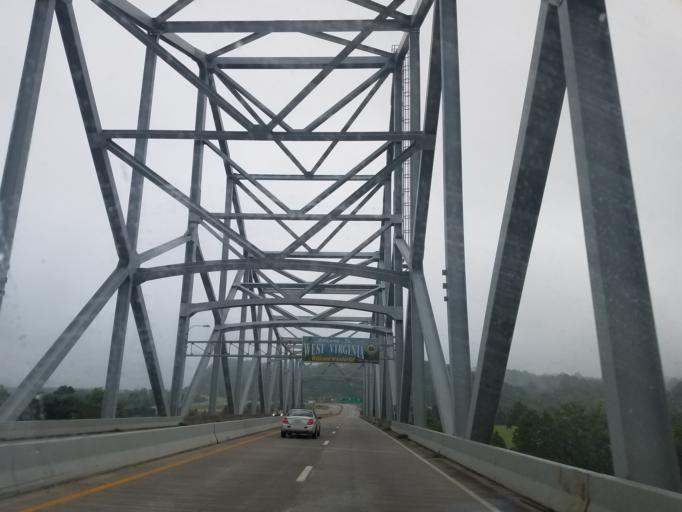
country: US
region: West Virginia
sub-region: Mason County
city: Point Pleasant
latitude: 38.8345
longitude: -82.1475
